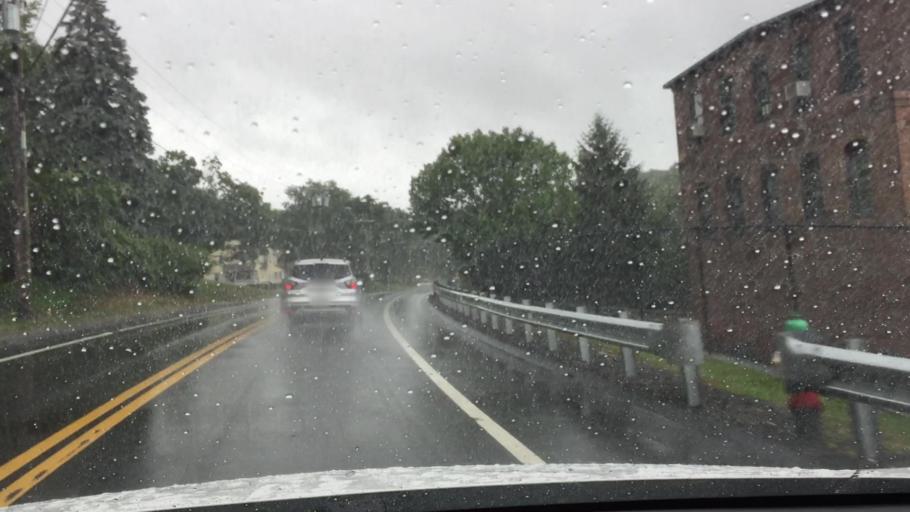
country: US
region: Massachusetts
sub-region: Berkshire County
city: Dalton
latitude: 42.4715
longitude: -73.1731
